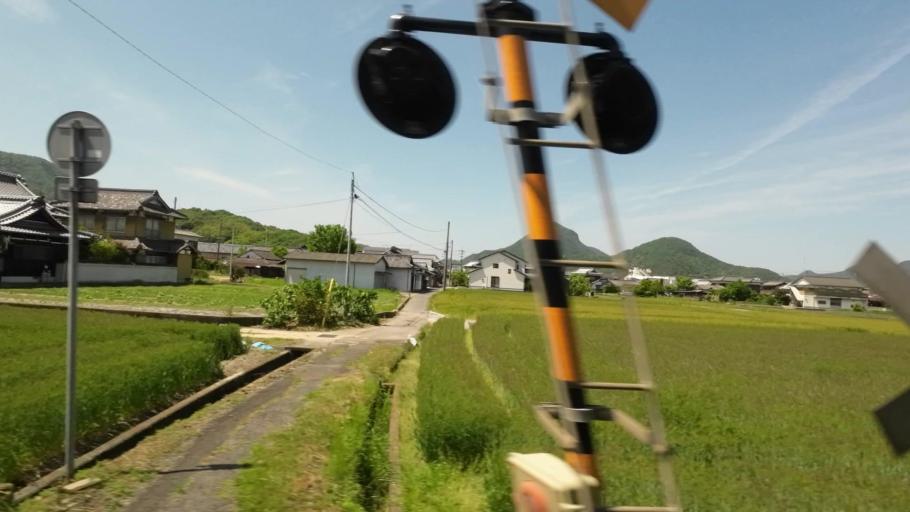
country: JP
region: Kagawa
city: Marugame
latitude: 34.2259
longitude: 133.7916
